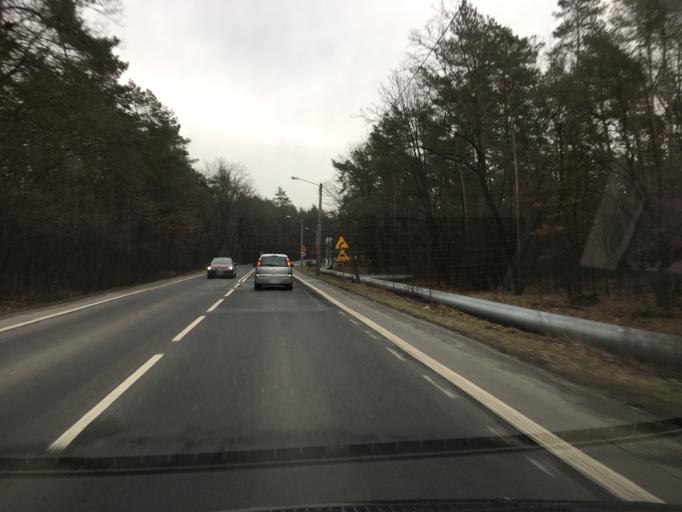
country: PL
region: Opole Voivodeship
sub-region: Powiat kedzierzynsko-kozielski
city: Kedzierzyn-Kozle
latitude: 50.3393
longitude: 18.2324
